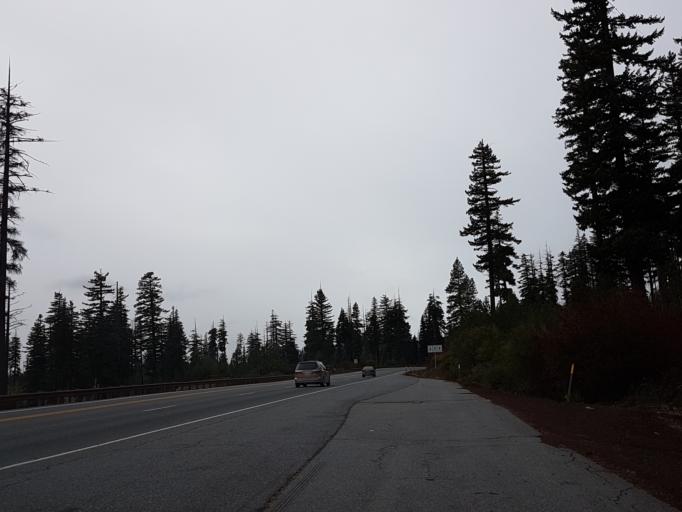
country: US
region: Oregon
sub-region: Deschutes County
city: Sisters
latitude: 44.4202
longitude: -121.7871
